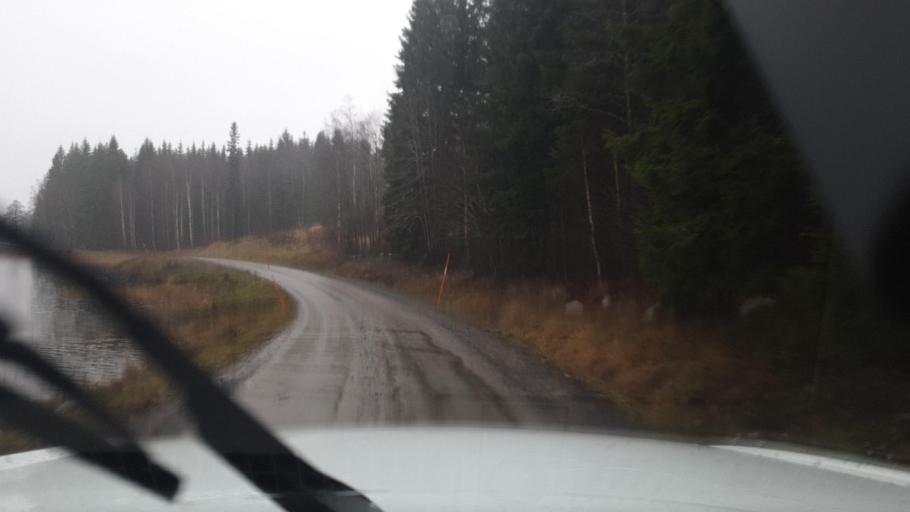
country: SE
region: Vaermland
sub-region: Arvika Kommun
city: Arvika
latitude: 59.8647
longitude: 12.8213
